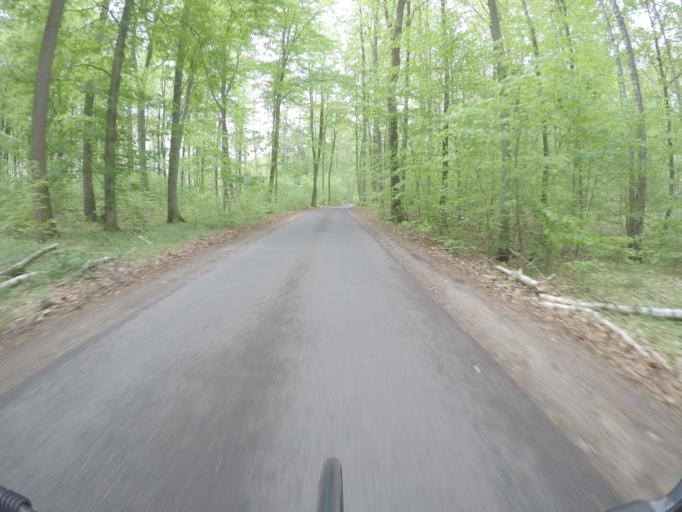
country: DE
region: Brandenburg
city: Marienwerder
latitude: 52.8998
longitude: 13.6639
